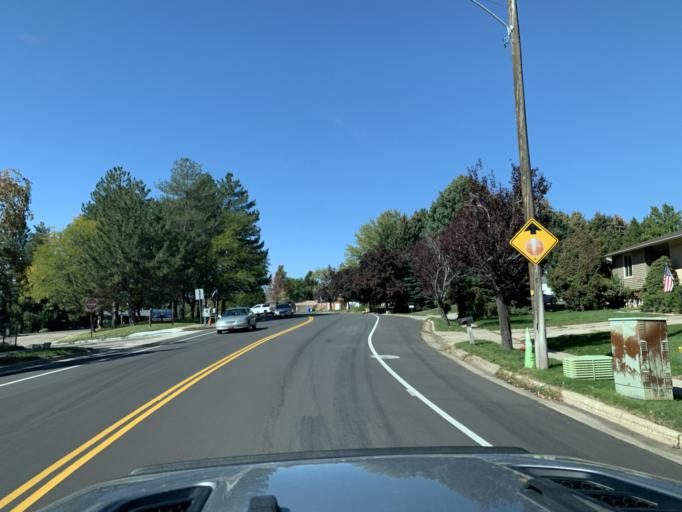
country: US
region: Utah
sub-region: Weber County
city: North Ogden
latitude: 41.3170
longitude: -111.9462
